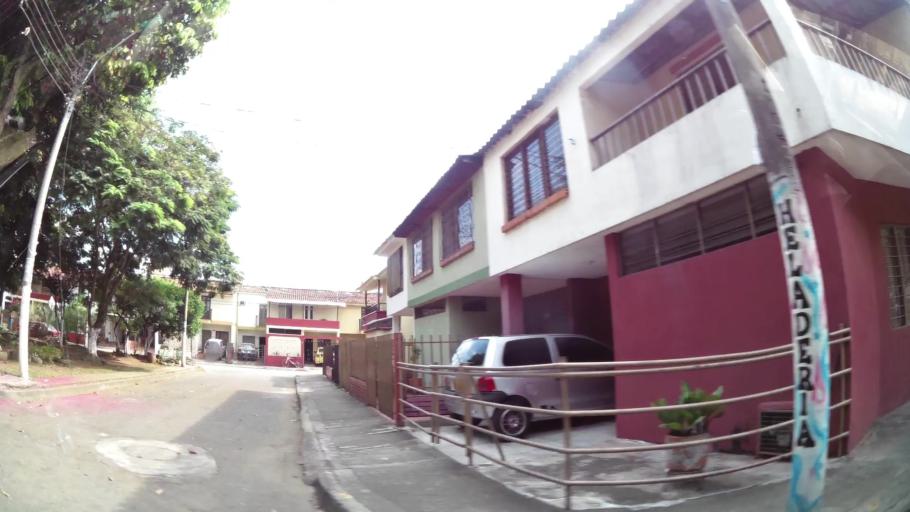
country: CO
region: Valle del Cauca
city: Cali
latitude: 3.4931
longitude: -76.4984
